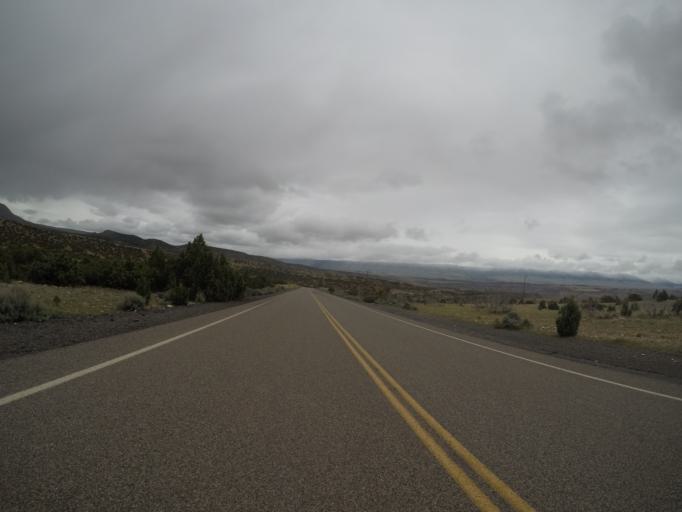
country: US
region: Wyoming
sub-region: Big Horn County
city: Lovell
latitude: 45.0994
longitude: -108.2464
